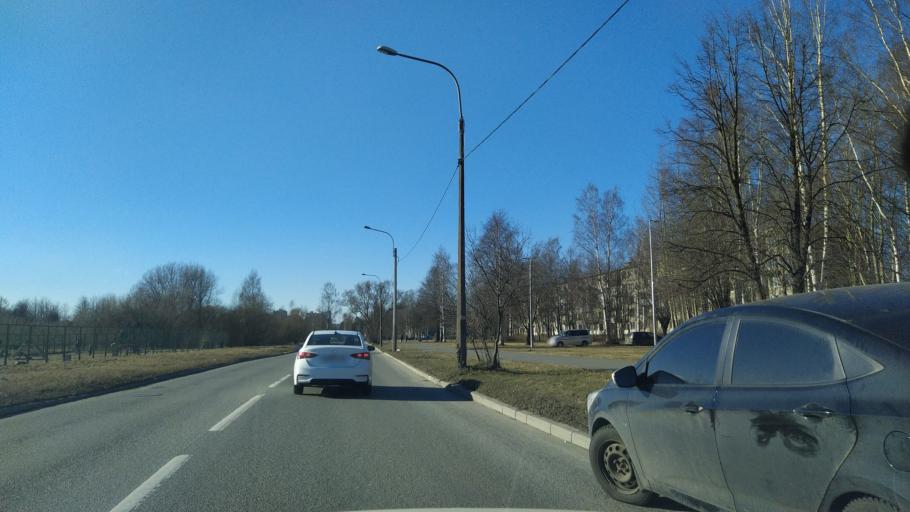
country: RU
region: Leningrad
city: Akademicheskoe
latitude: 59.9983
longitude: 30.4313
